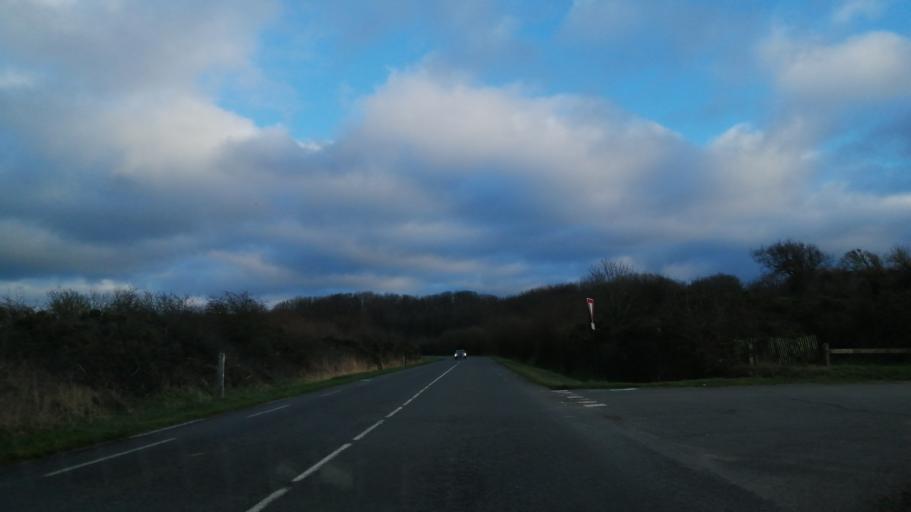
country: FR
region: Nord-Pas-de-Calais
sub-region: Departement du Pas-de-Calais
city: Wissant
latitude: 50.8738
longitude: 1.6537
